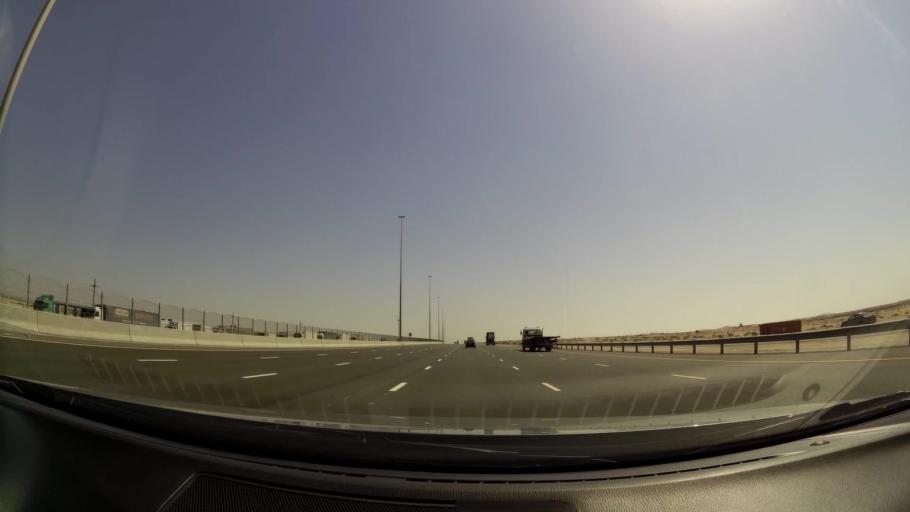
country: AE
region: Dubai
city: Dubai
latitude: 24.9338
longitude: 55.1201
